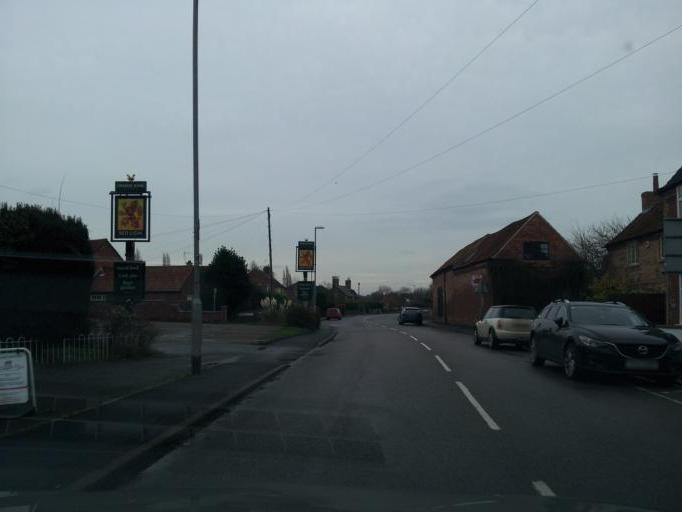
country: GB
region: England
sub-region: Lincolnshire
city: Long Bennington
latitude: 52.9419
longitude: -0.8011
